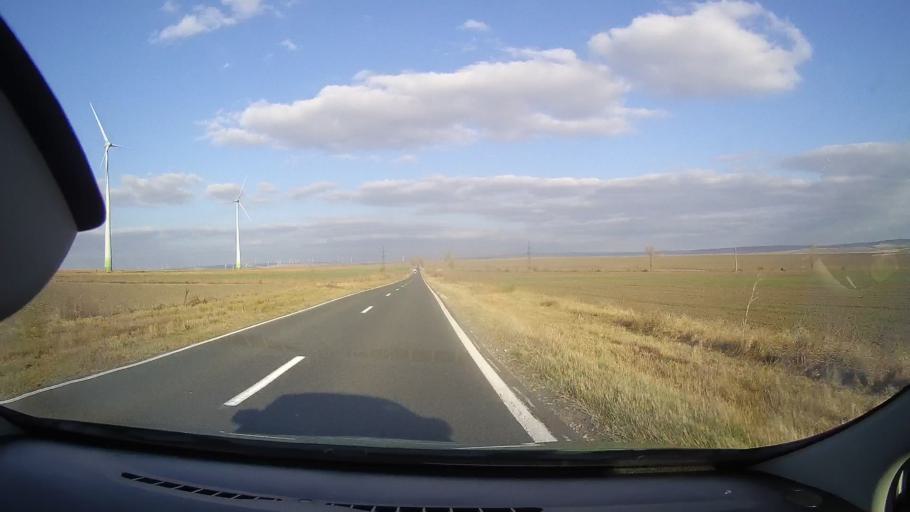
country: RO
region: Tulcea
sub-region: Comuna Topolog
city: Topolog
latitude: 44.8227
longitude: 28.2682
